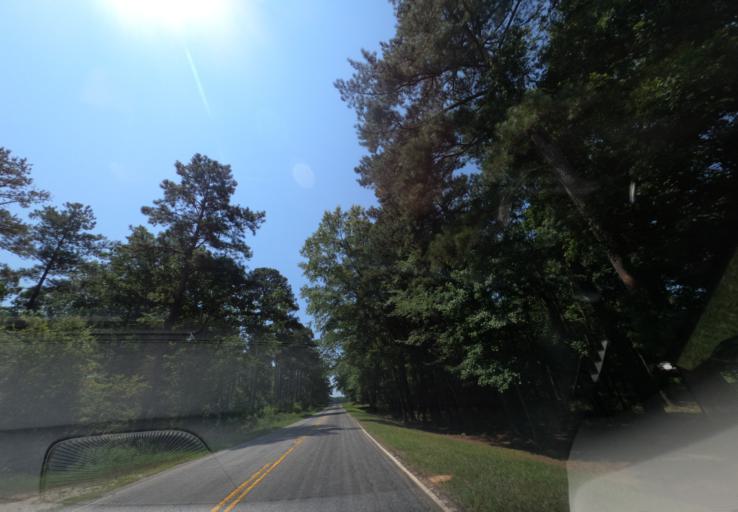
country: US
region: South Carolina
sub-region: McCormick County
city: McCormick
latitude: 33.9843
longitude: -82.1299
